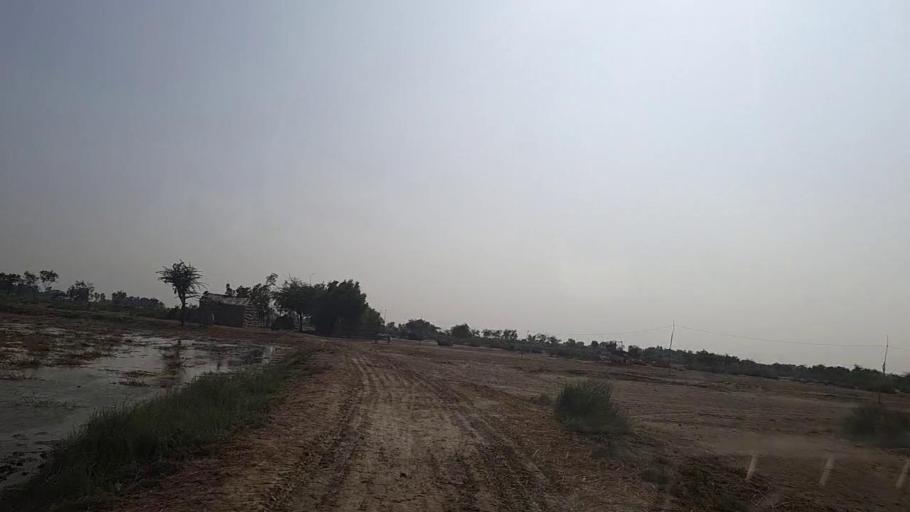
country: PK
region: Sindh
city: Mirpur Sakro
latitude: 24.5675
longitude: 67.8168
